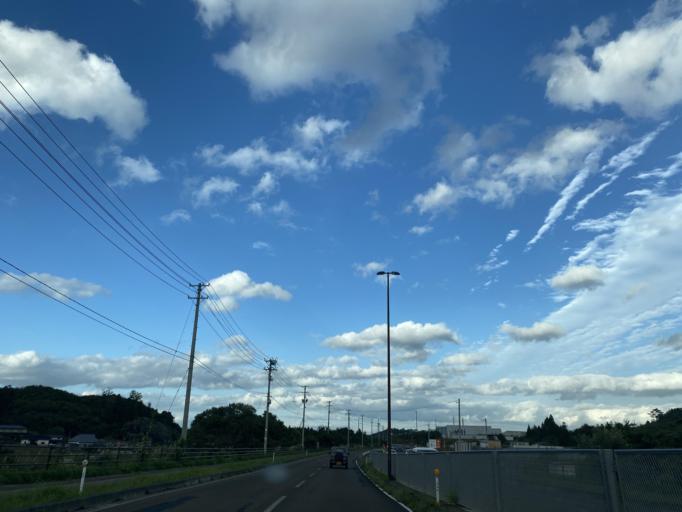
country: JP
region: Miyagi
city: Tomiya
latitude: 38.3593
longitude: 140.8465
